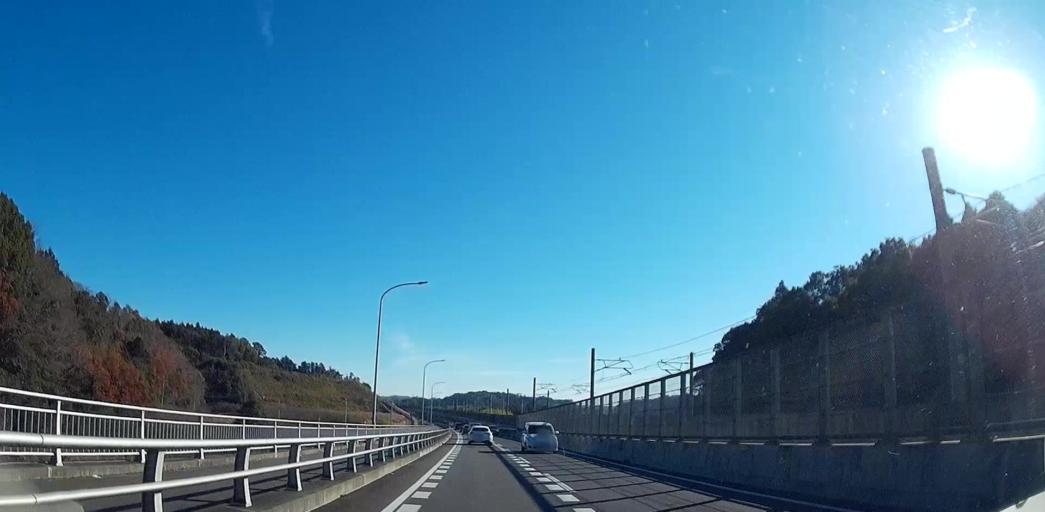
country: JP
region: Chiba
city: Sakura
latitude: 35.7833
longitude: 140.2283
